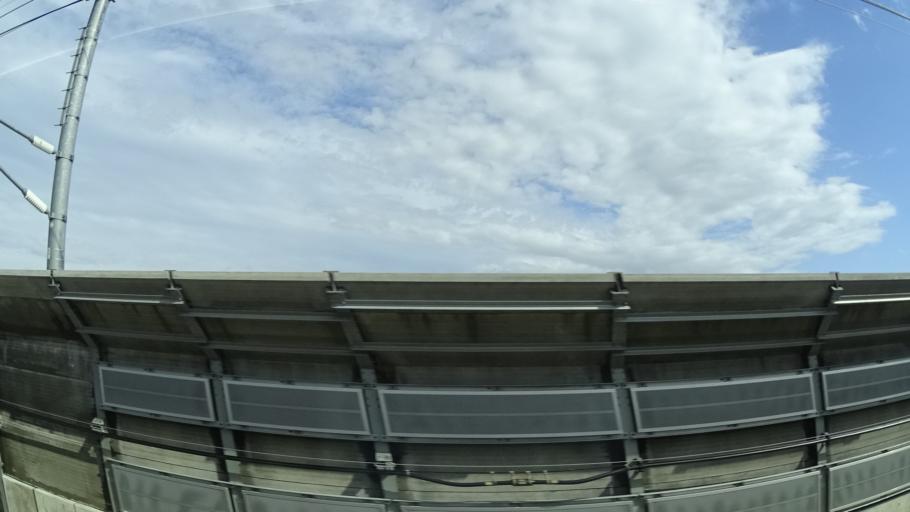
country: JP
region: Toyama
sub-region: Oyabe Shi
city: Oyabe
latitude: 36.6747
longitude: 136.8994
